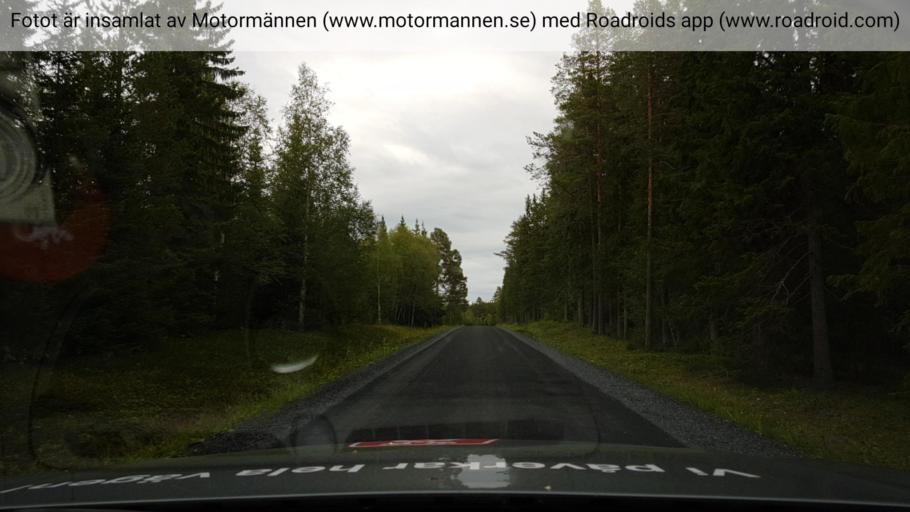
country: SE
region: Jaemtland
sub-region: Krokoms Kommun
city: Valla
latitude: 63.3658
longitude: 13.9327
